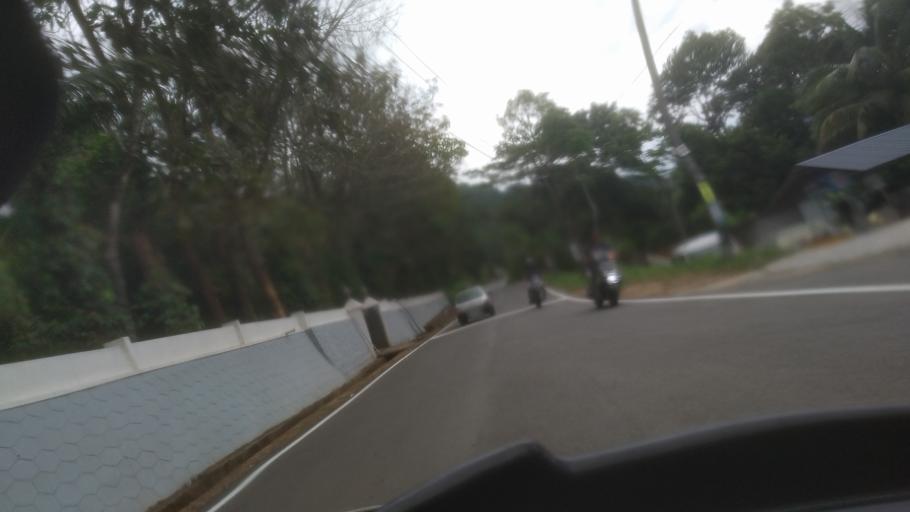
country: IN
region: Kerala
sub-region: Idukki
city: Idukki
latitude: 9.9446
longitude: 77.0181
